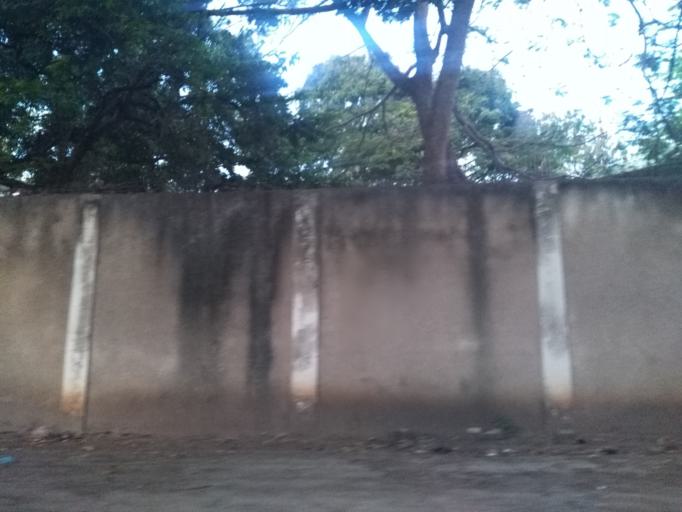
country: TZ
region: Dar es Salaam
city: Magomeni
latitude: -6.7860
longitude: 39.2719
